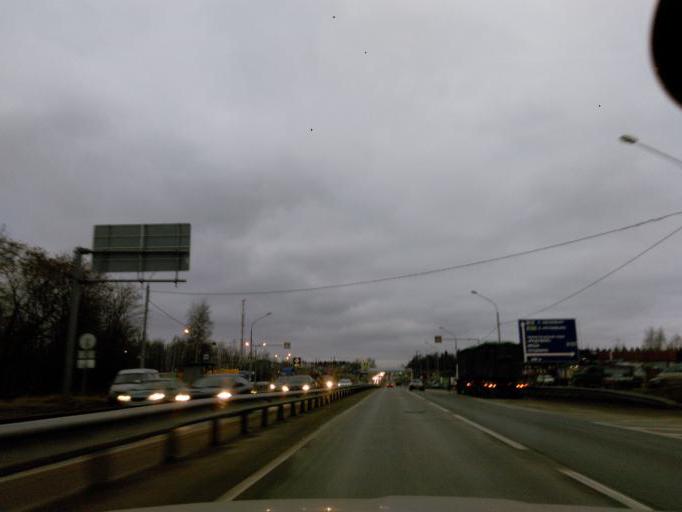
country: RU
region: Moskovskaya
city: Radumlya
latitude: 56.0682
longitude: 37.1358
